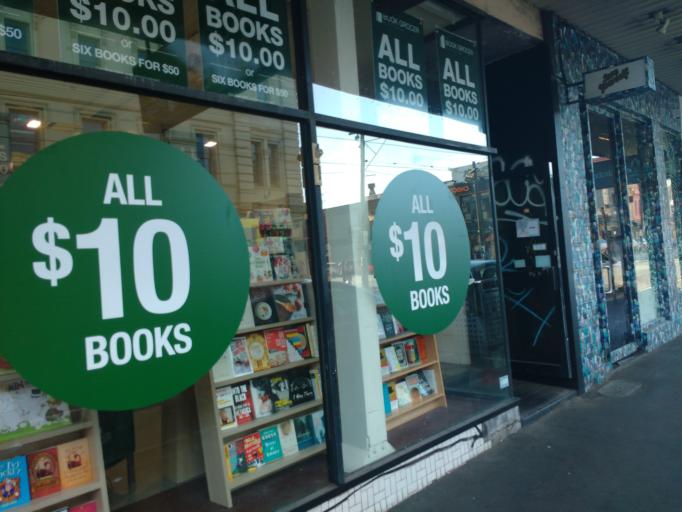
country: AU
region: Victoria
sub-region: Yarra
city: Fitzroy
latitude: -37.7987
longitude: 144.9783
